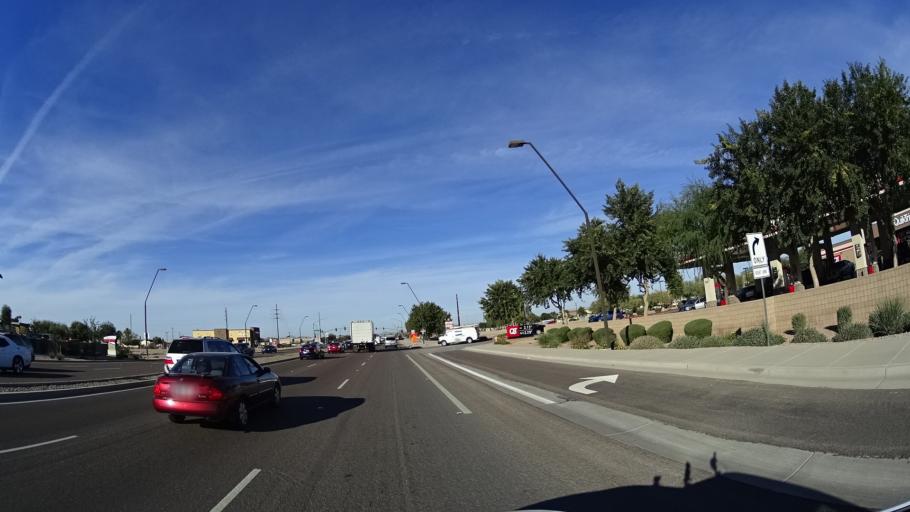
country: US
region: Arizona
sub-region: Maricopa County
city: Queen Creek
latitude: 33.2468
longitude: -111.6377
